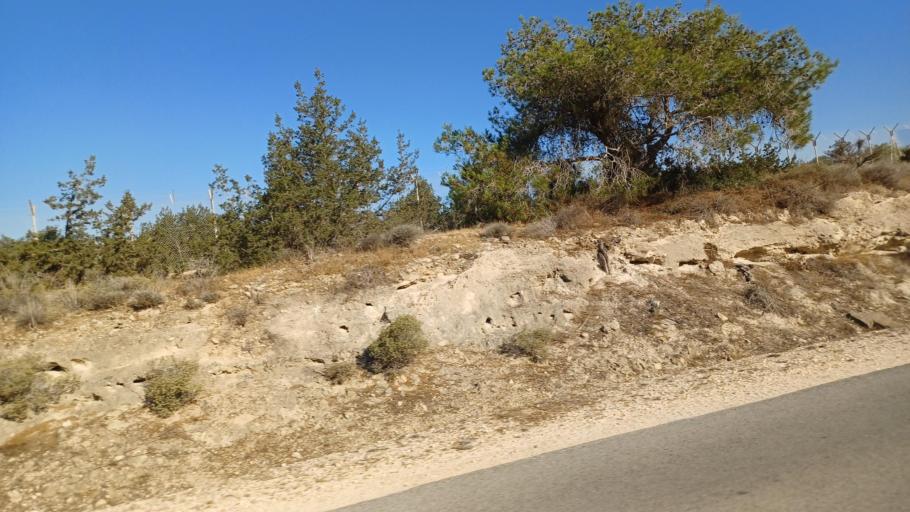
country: CY
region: Larnaka
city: Xylotymbou
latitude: 34.9916
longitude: 33.7421
